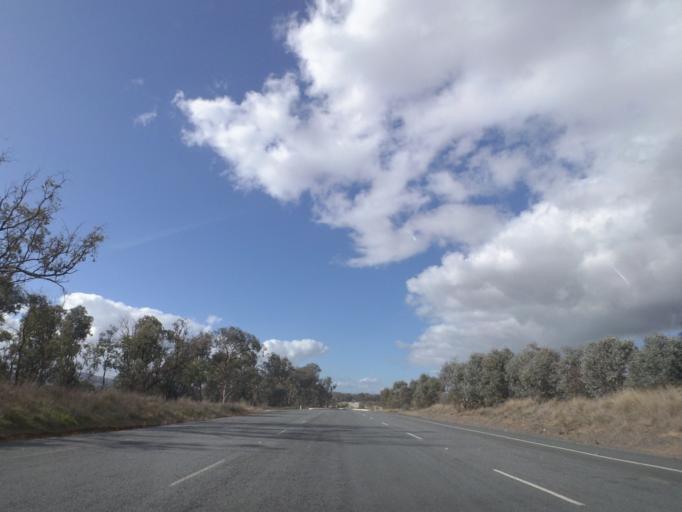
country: AU
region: New South Wales
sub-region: Greater Hume Shire
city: Holbrook
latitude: -35.6813
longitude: 147.3636
